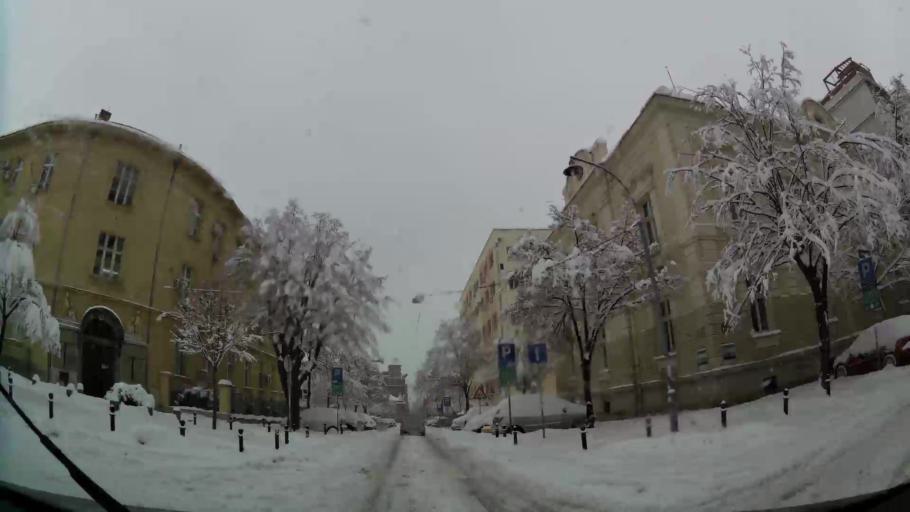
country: RS
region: Central Serbia
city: Belgrade
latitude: 44.8009
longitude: 20.4625
